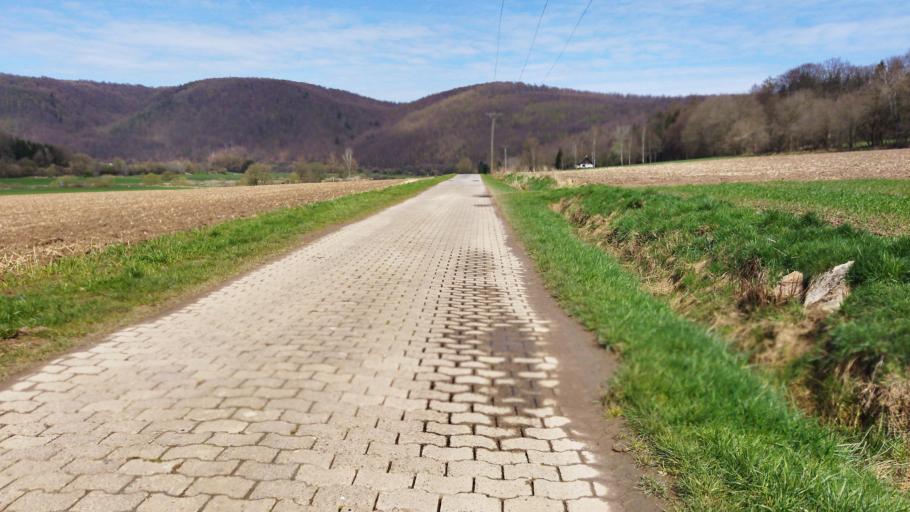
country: DE
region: Lower Saxony
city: Bad Karlshafen
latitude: 51.6439
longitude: 9.4984
